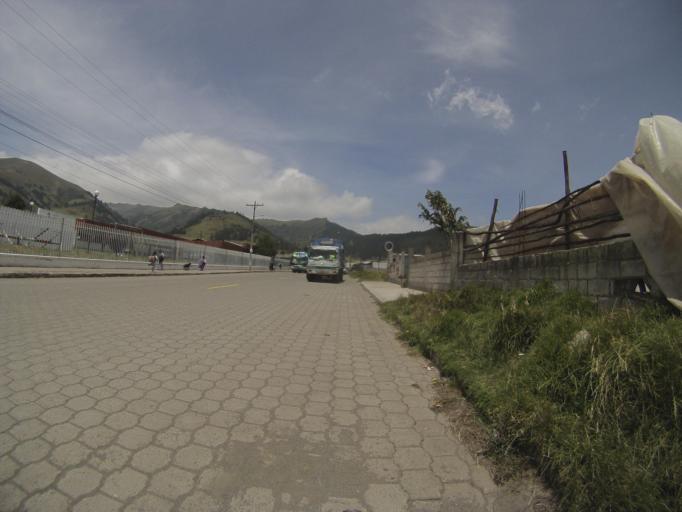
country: EC
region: Pichincha
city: Cayambe
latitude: 0.1527
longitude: -78.0694
